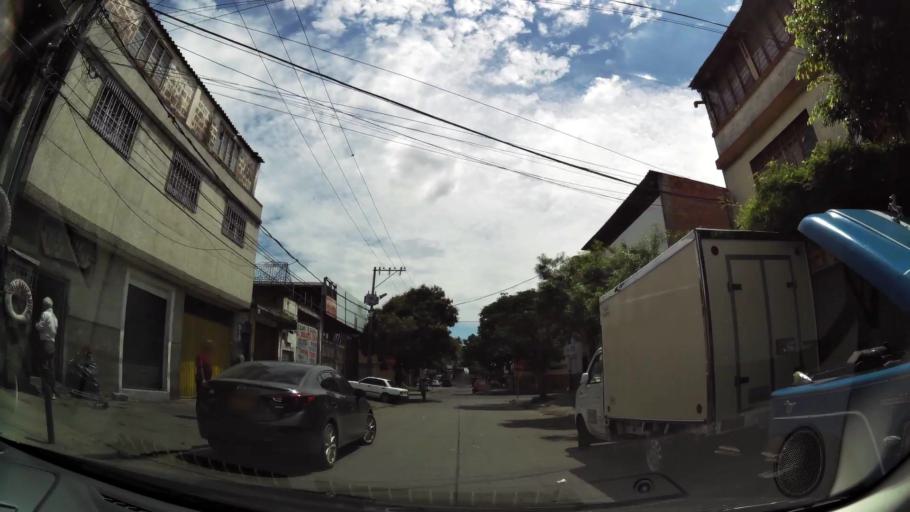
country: CO
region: Valle del Cauca
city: Cali
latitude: 3.4457
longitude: -76.5198
